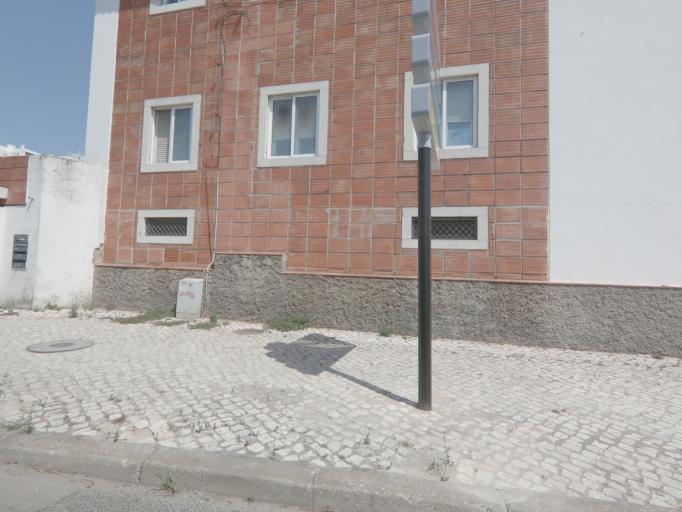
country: PT
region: Setubal
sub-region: Setubal
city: Setubal
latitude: 38.5361
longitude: -8.8845
